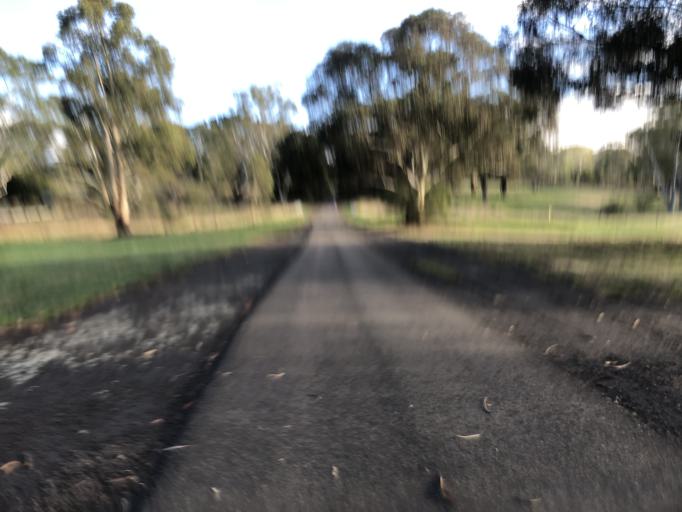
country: AU
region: New South Wales
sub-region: Orange Municipality
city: Orange
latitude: -33.3248
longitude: 149.0861
